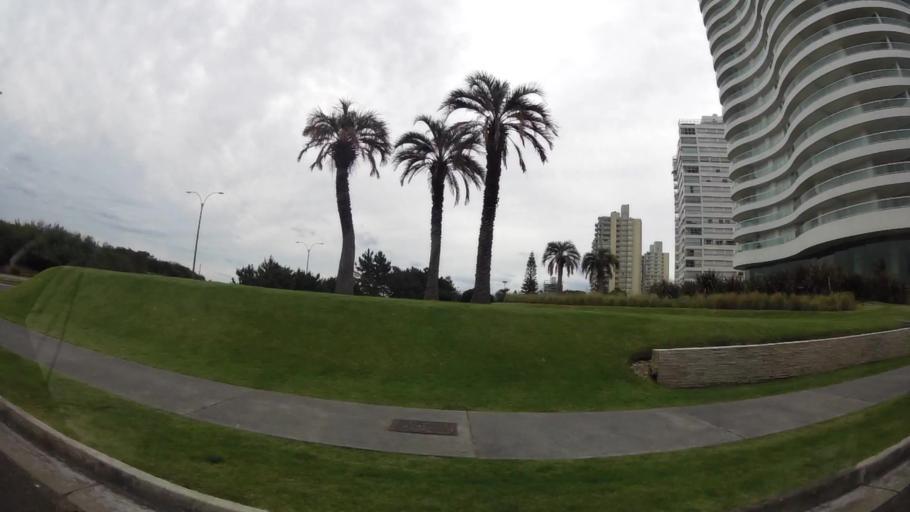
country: UY
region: Maldonado
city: Maldonado
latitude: -34.9280
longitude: -54.9605
